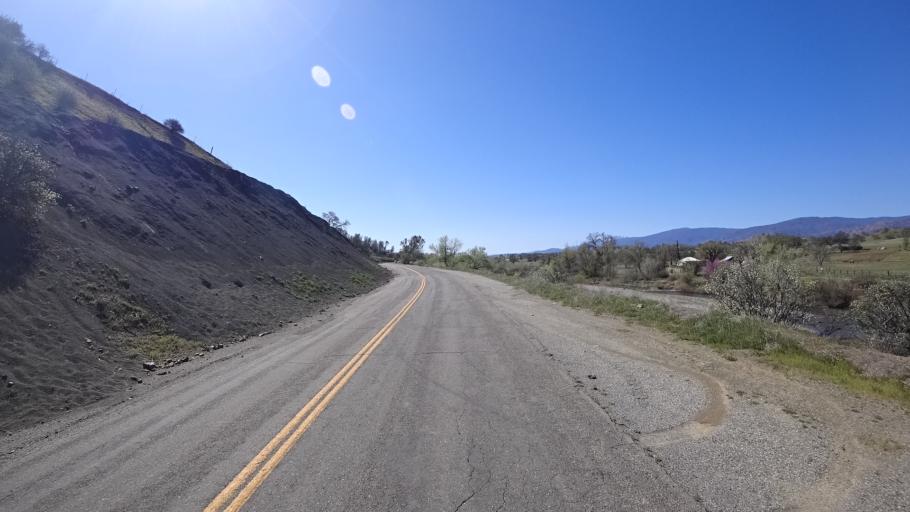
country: US
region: California
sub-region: Glenn County
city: Orland
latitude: 39.6771
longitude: -122.5243
